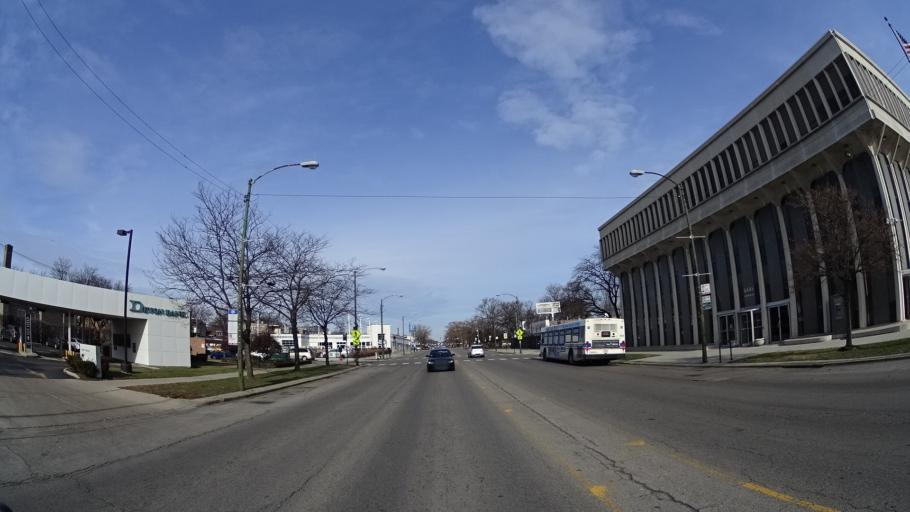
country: US
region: Illinois
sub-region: Cook County
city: Lincolnwood
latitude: 41.9992
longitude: -87.6900
